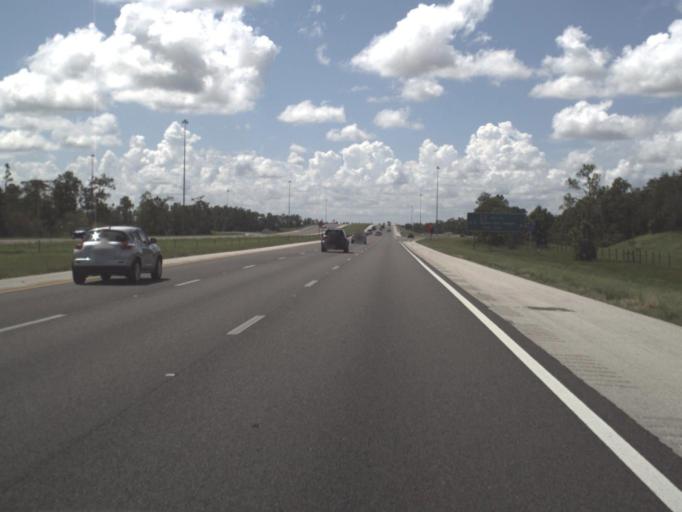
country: US
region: Florida
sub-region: Lee County
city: Gateway
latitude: 26.5544
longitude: -81.7953
